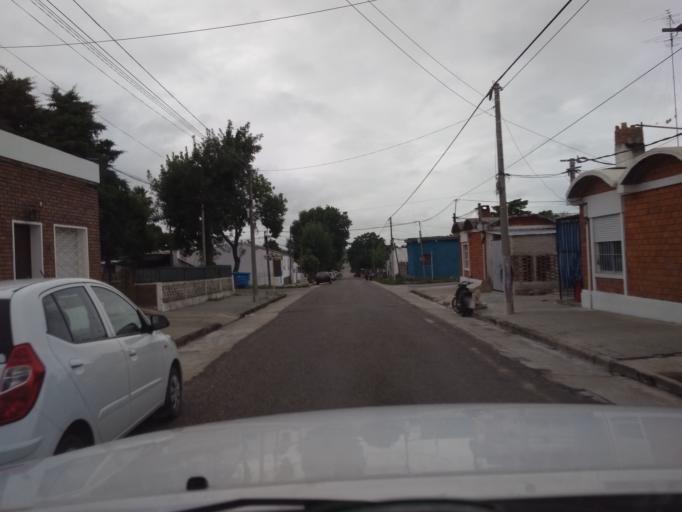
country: UY
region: Florida
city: Florida
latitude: -34.1045
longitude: -56.2111
